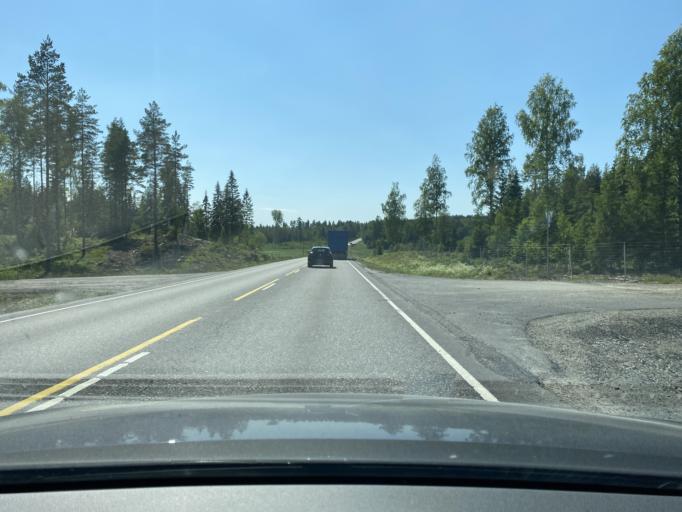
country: FI
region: Pirkanmaa
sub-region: Lounais-Pirkanmaa
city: Mouhijaervi
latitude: 61.3925
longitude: 23.2260
